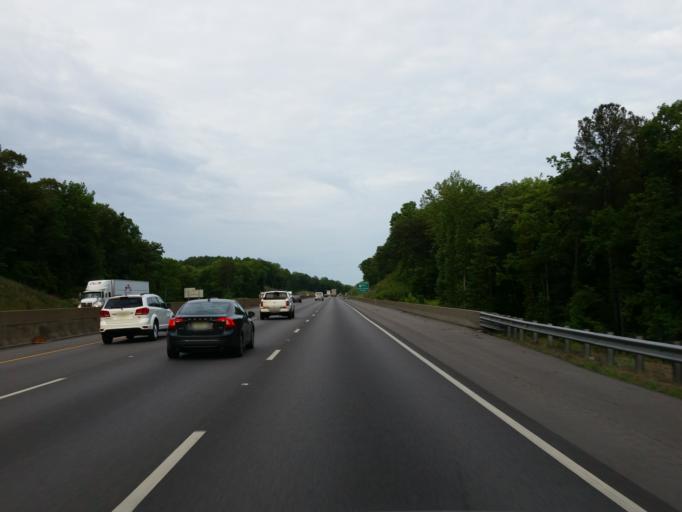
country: US
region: Alabama
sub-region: Saint Clair County
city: Odenville
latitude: 33.5960
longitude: -86.3846
